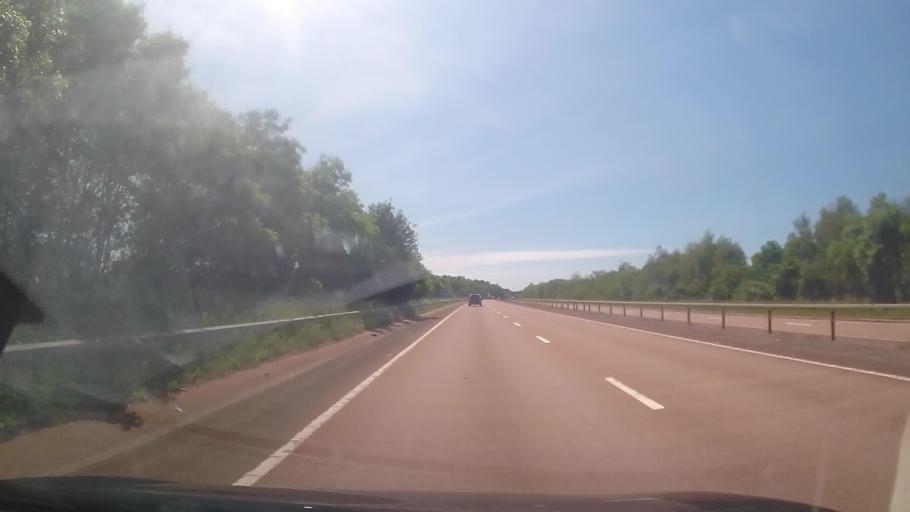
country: GB
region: England
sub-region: Devon
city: Topsham
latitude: 50.7286
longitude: -3.4019
